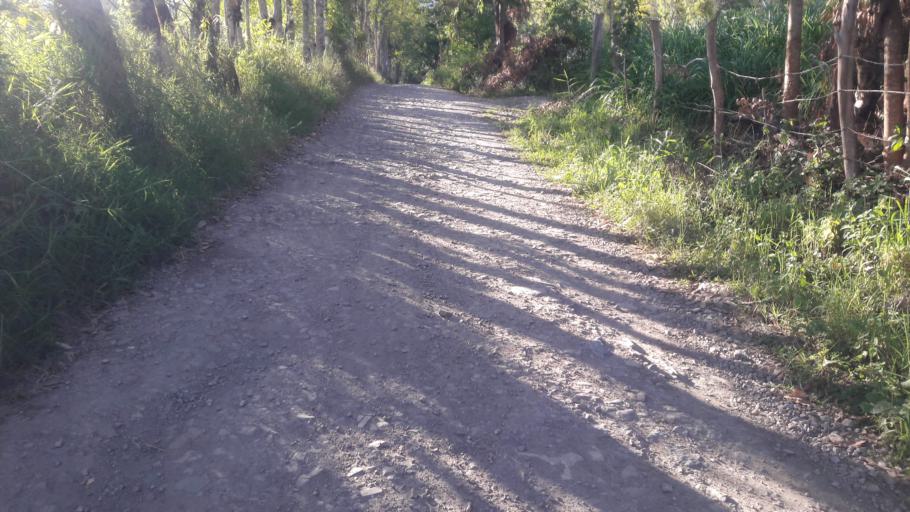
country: CO
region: Cundinamarca
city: Tenza
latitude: 5.0884
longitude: -73.4248
